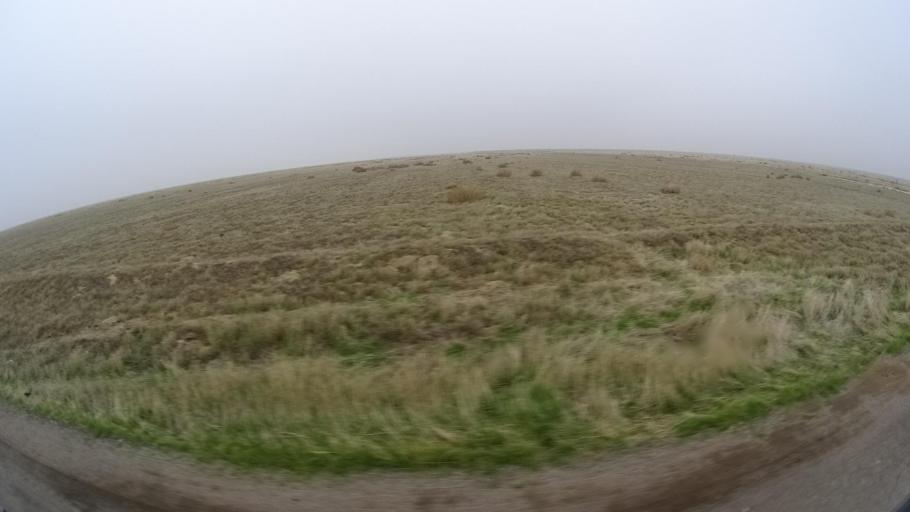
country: US
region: California
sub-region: Tulare County
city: Alpaugh
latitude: 35.7835
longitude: -119.4011
